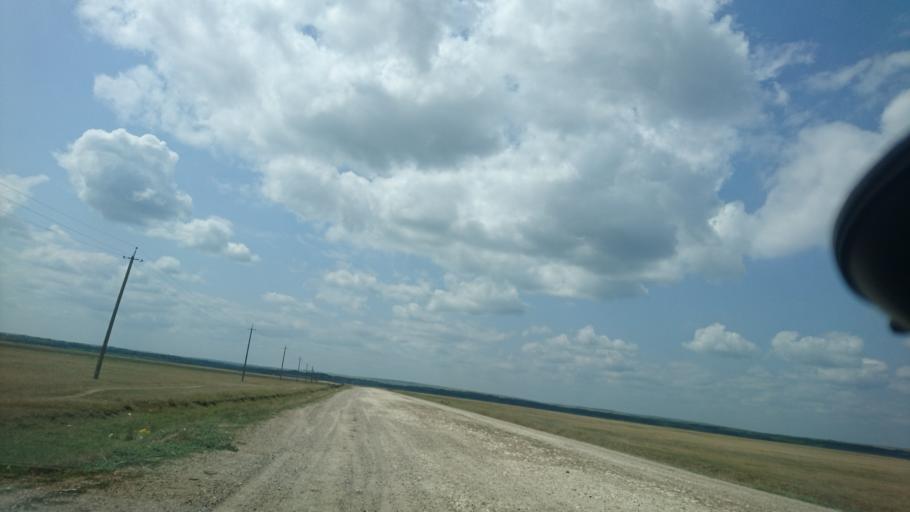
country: RO
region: Iasi
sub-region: Comuna Bivolari
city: Bivolari
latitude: 47.5588
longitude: 27.4813
